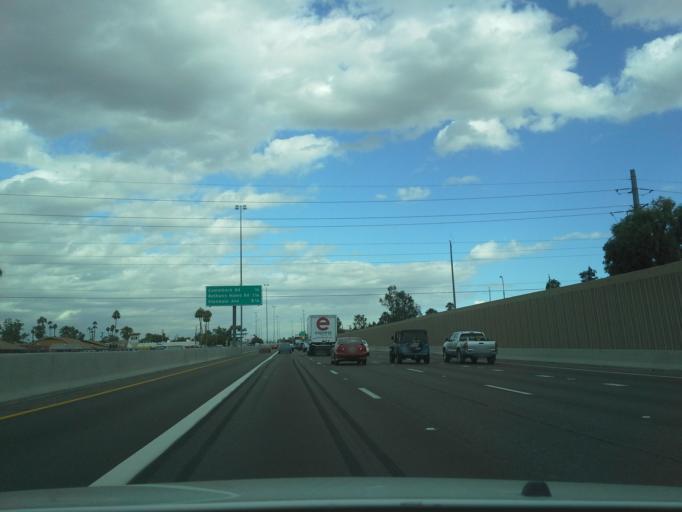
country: US
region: Arizona
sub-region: Maricopa County
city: Phoenix
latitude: 33.5016
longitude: -112.1128
